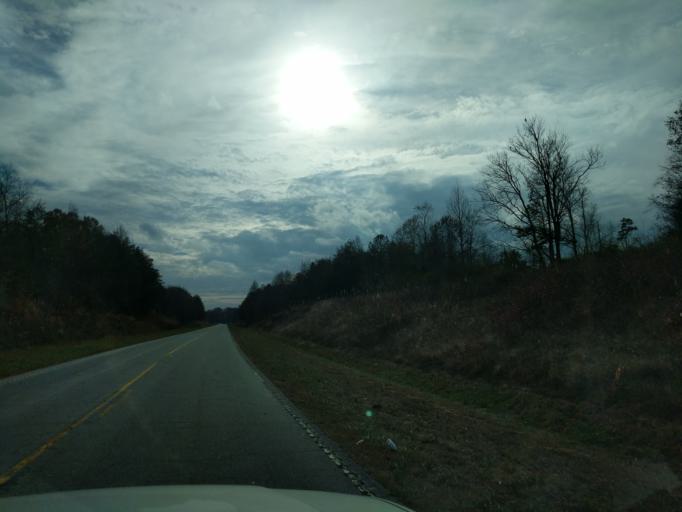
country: US
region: Georgia
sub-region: Franklin County
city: Gumlog
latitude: 34.5678
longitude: -83.0483
